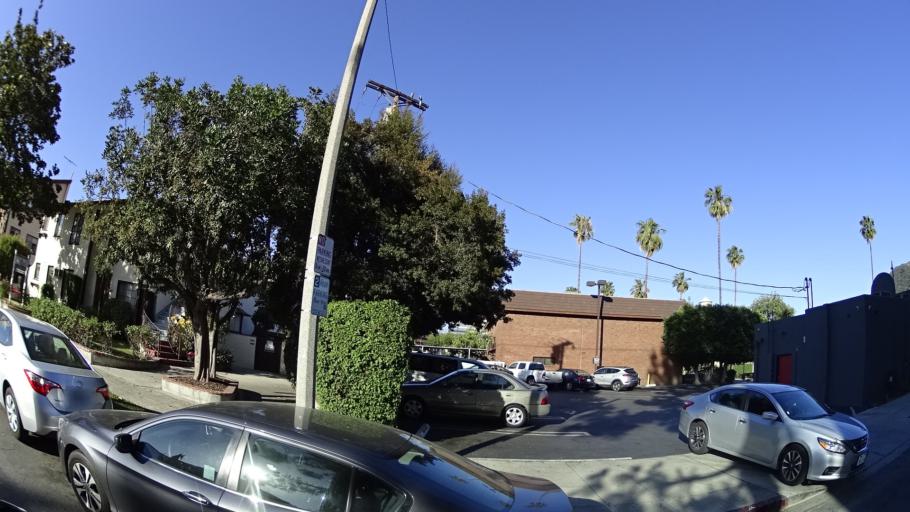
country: US
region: California
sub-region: Los Angeles County
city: Universal City
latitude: 34.1512
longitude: -118.3413
